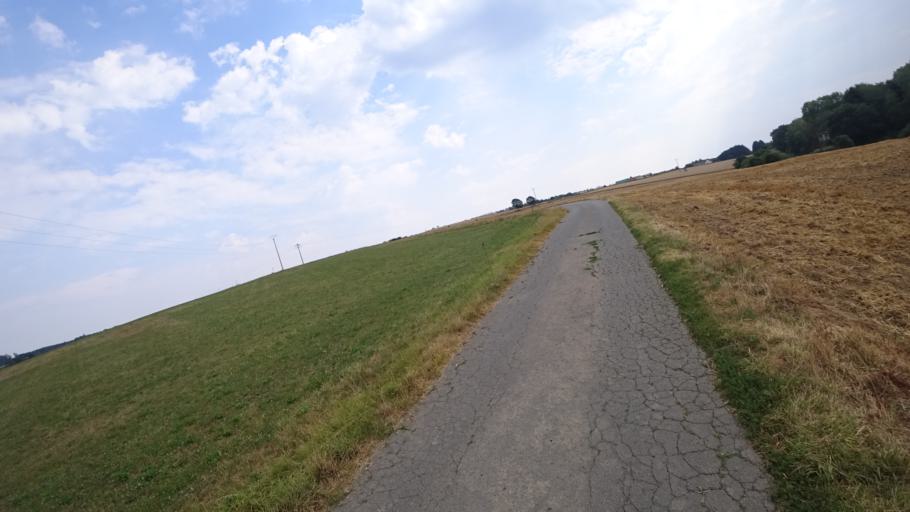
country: DE
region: Rheinland-Pfalz
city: Hohr-Grenzhausen
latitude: 50.4172
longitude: 7.6739
